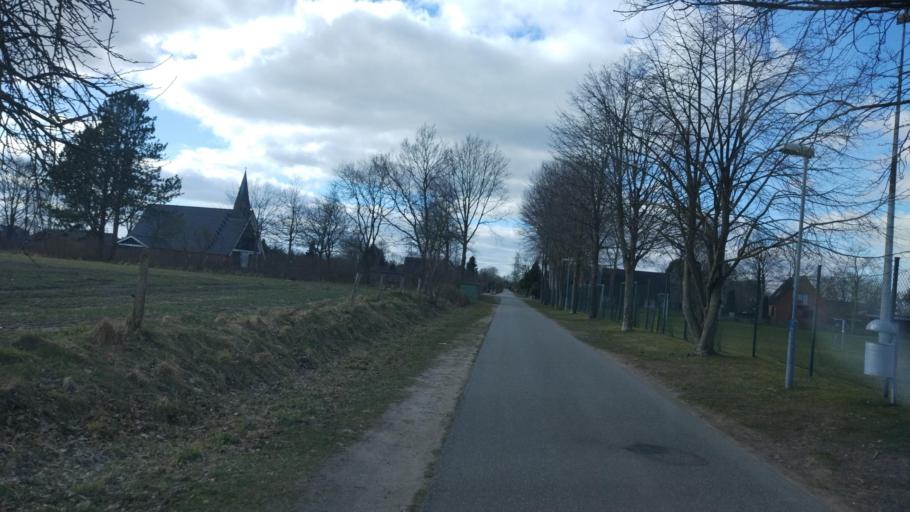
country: DE
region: Schleswig-Holstein
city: Gross Rheide
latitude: 54.4406
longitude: 9.4342
